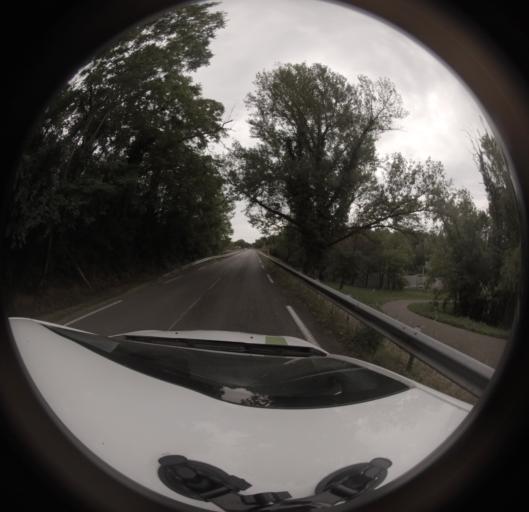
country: FR
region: Midi-Pyrenees
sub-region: Departement du Tarn-et-Garonne
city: Montauban
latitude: 44.0032
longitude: 1.3777
